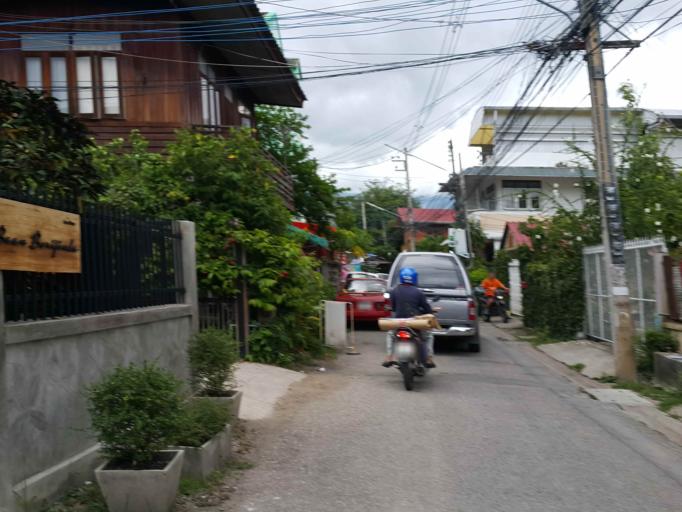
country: TH
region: Chiang Mai
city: Chiang Mai
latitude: 18.7942
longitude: 98.9910
